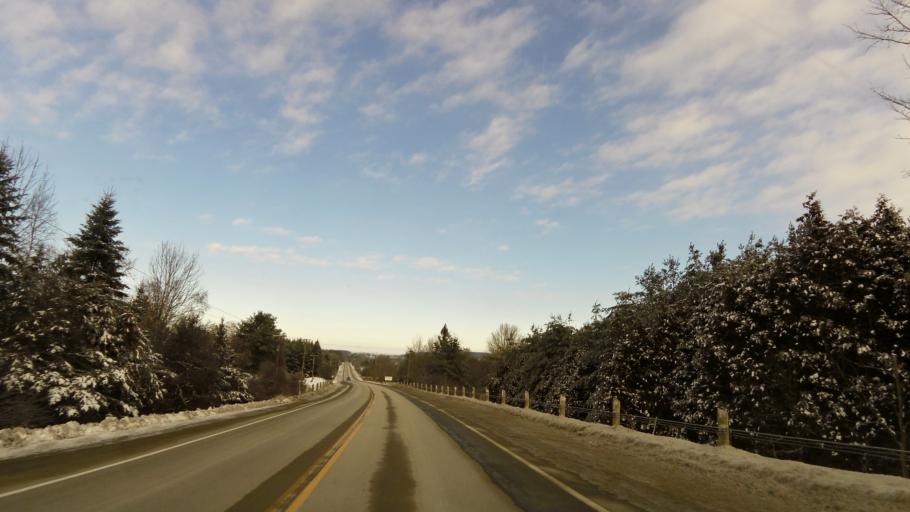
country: CA
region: Ontario
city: Quinte West
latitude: 44.1165
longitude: -77.7802
